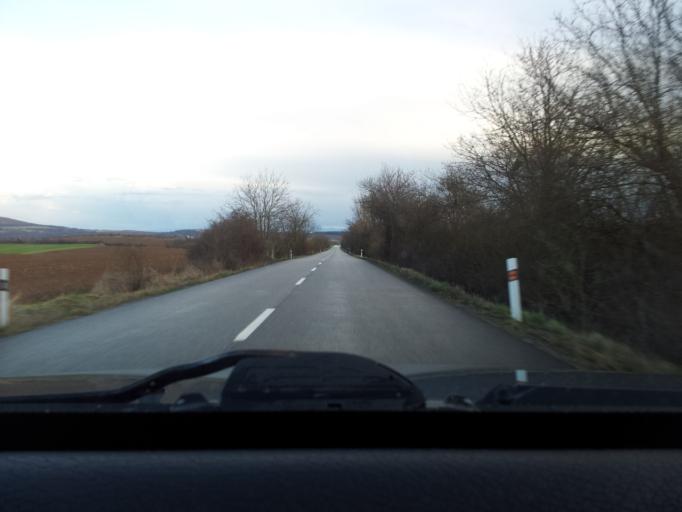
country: SK
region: Nitriansky
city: Tlmace
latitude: 48.3383
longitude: 18.4885
